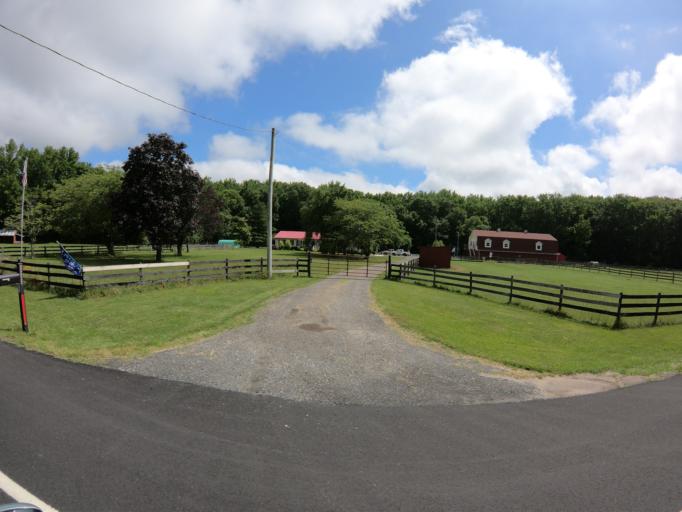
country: US
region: Maryland
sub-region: Caroline County
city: Greensboro
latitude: 39.0431
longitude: -75.8052
